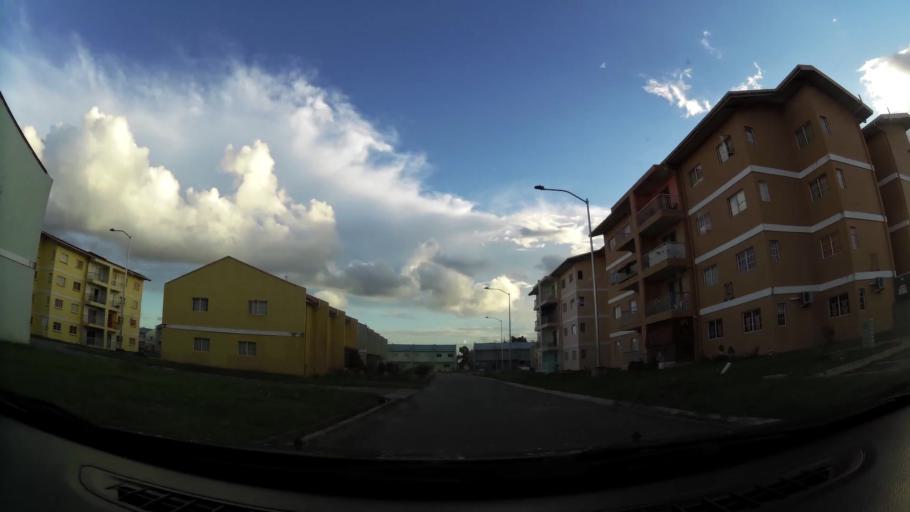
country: TT
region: Tunapuna/Piarco
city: Arouca
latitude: 10.6122
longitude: -61.3561
